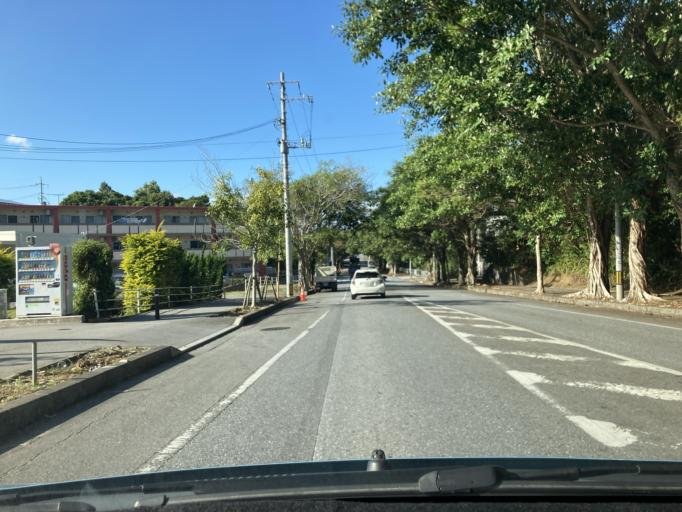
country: JP
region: Okinawa
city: Gushikawa
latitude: 26.3639
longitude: 127.8424
